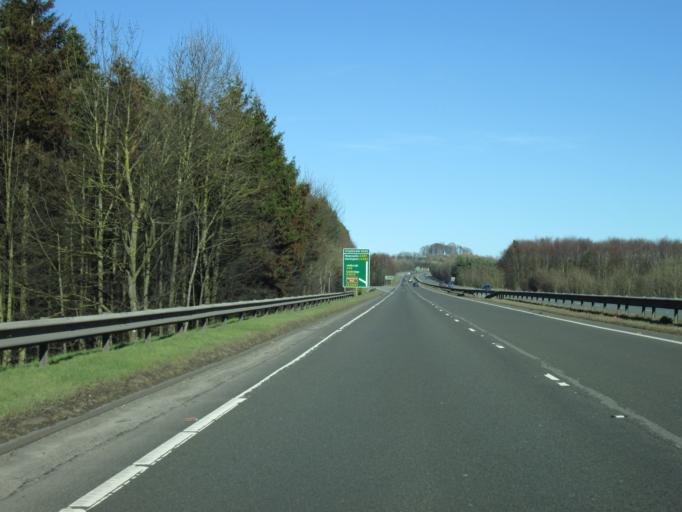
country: GB
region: England
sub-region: Northumberland
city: Corbridge
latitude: 54.9817
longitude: -2.0330
